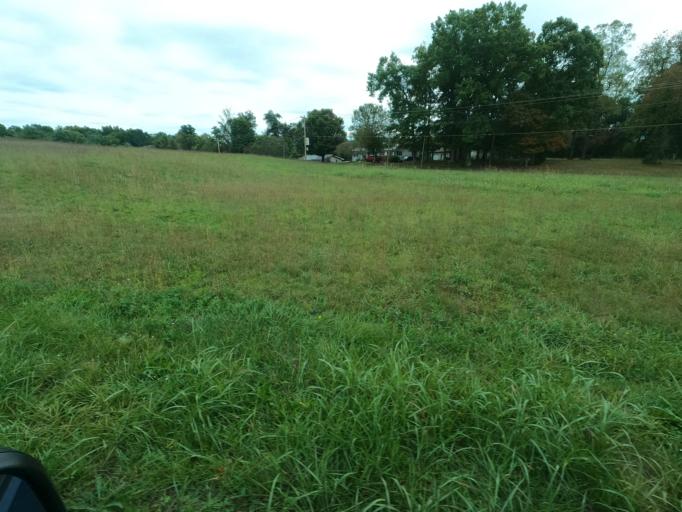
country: US
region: Tennessee
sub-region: Washington County
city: Jonesborough
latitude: 36.2253
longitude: -82.5898
